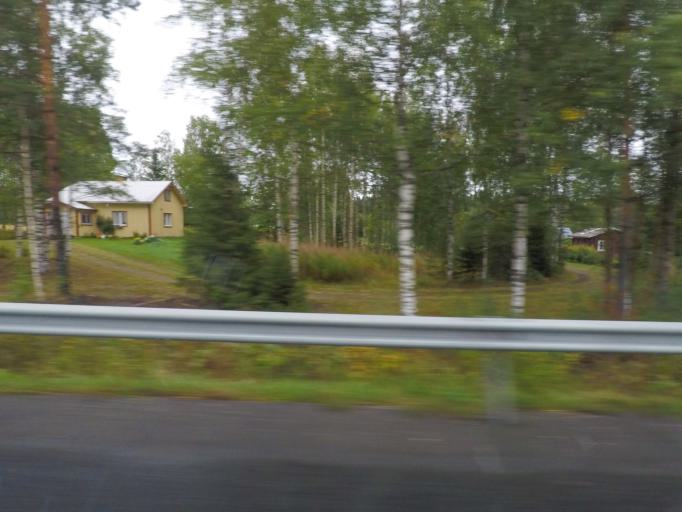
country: FI
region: Northern Savo
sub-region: Varkaus
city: Leppaevirta
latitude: 62.4970
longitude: 27.7527
